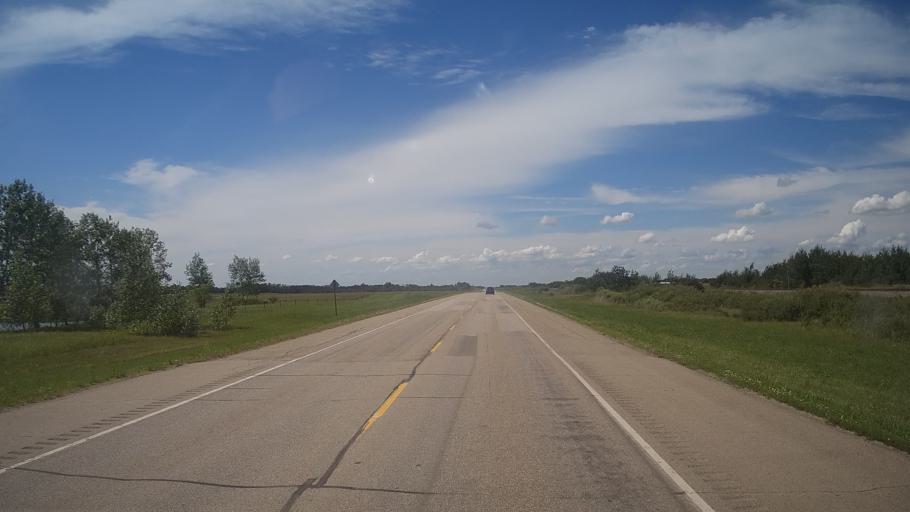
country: CA
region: Saskatchewan
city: Yorkton
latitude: 51.0496
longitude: -102.1813
